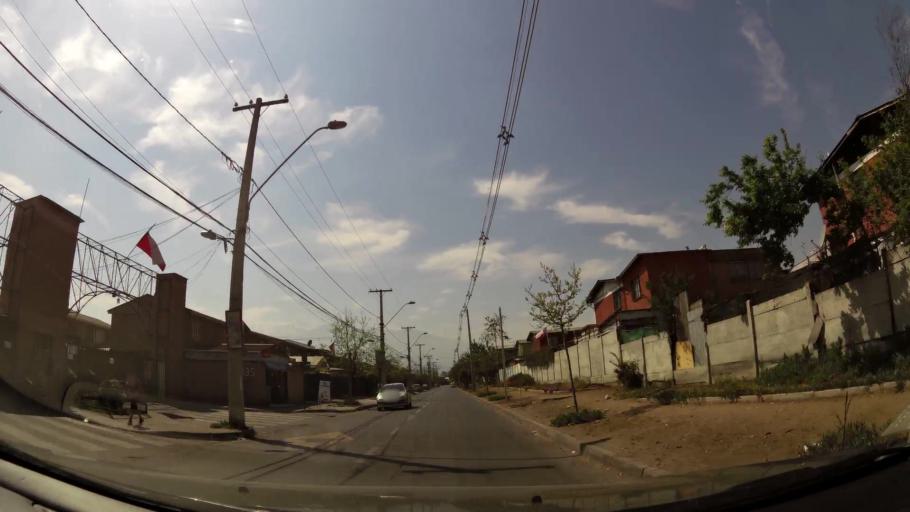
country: CL
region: Santiago Metropolitan
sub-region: Provincia de Santiago
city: La Pintana
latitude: -33.5786
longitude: -70.6004
